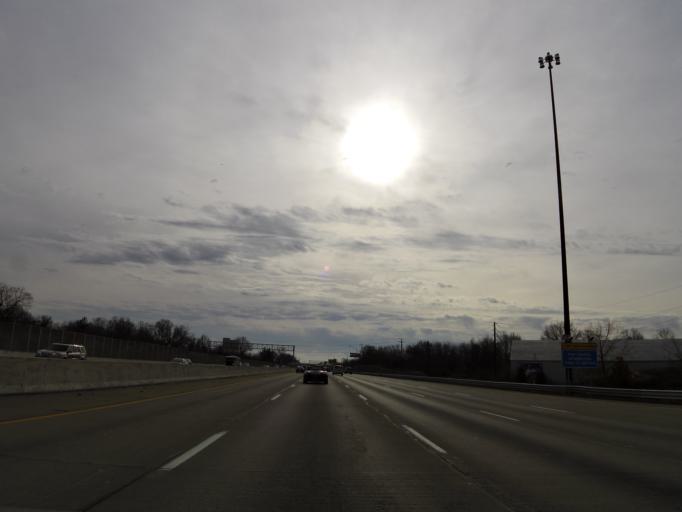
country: US
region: Indiana
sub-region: Marion County
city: Lawrence
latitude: 39.8457
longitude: -86.0435
